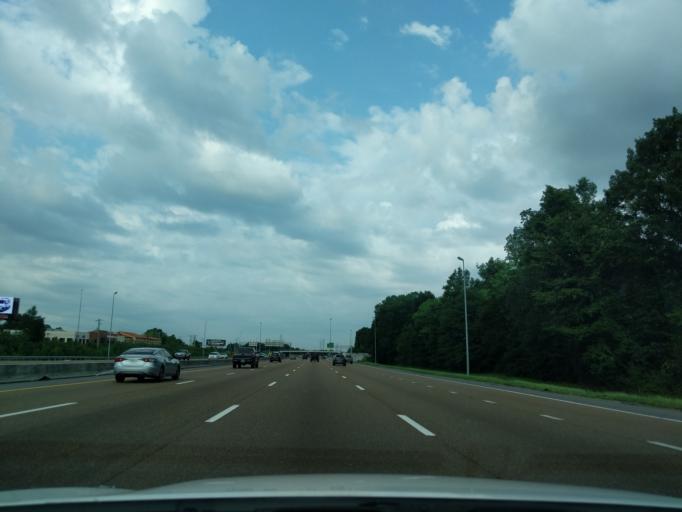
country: US
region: Tennessee
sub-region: Shelby County
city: Germantown
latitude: 35.0811
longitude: -89.9001
